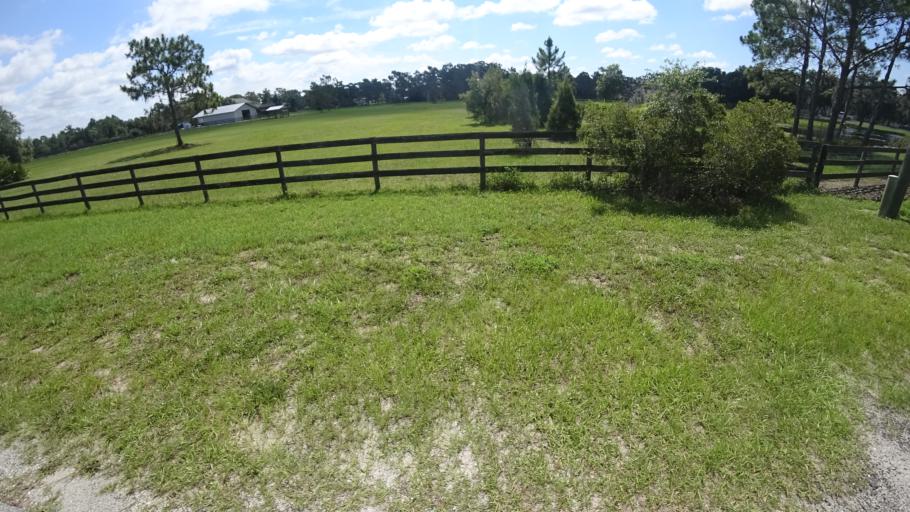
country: US
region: Florida
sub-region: Sarasota County
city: The Meadows
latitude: 27.4150
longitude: -82.3265
